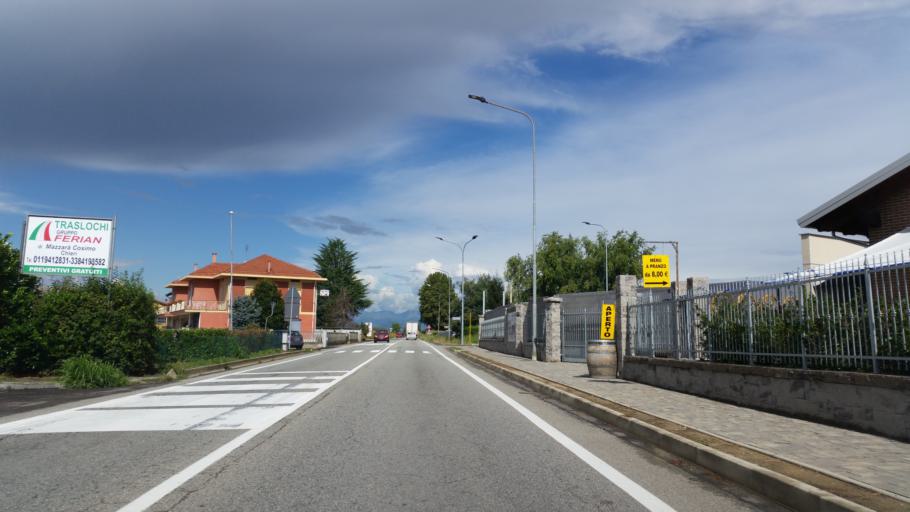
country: IT
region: Piedmont
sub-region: Provincia di Torino
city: Marocchi
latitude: 44.9434
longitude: 7.8141
